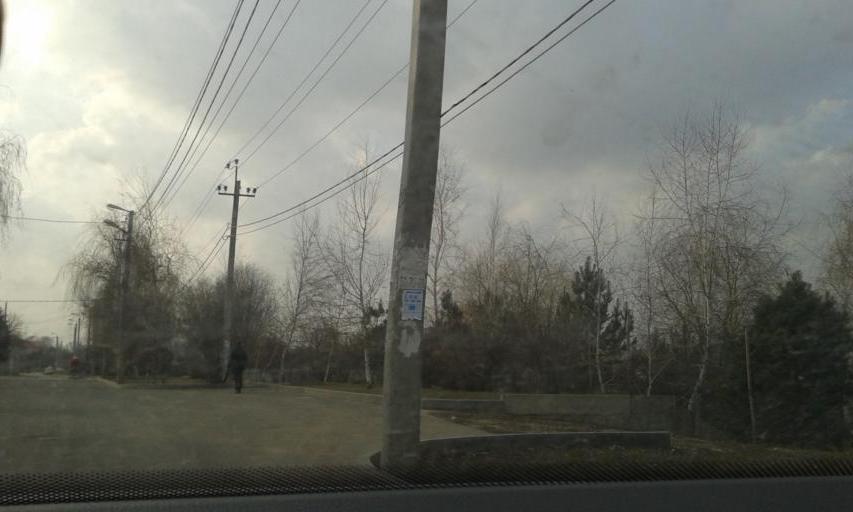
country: RU
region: Volgograd
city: Volgograd
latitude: 48.6560
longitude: 44.4266
